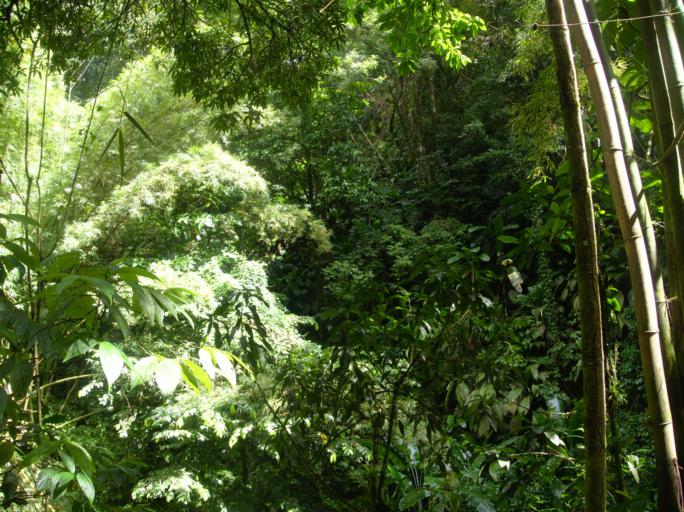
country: MQ
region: Martinique
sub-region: Martinique
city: Saint-Joseph
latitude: 14.6748
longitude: -61.0951
